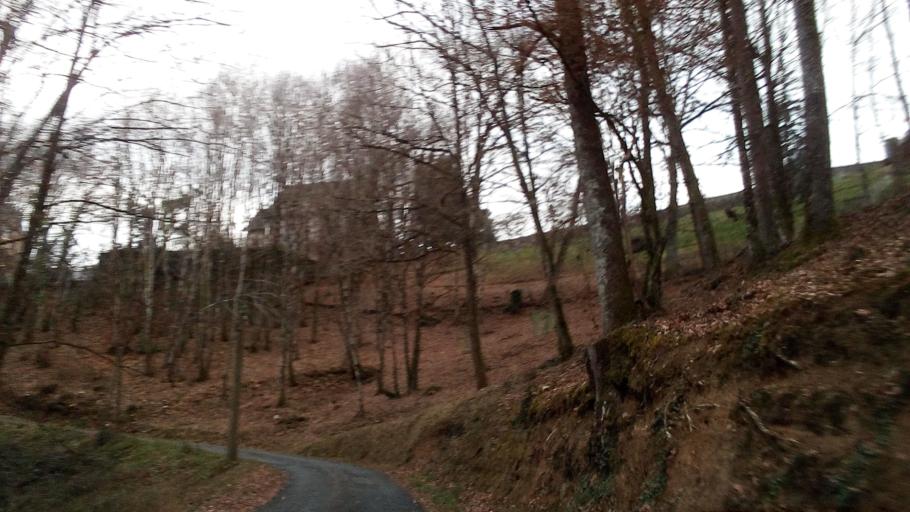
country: FR
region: Limousin
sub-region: Departement de la Correze
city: Naves
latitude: 45.3115
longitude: 1.7736
